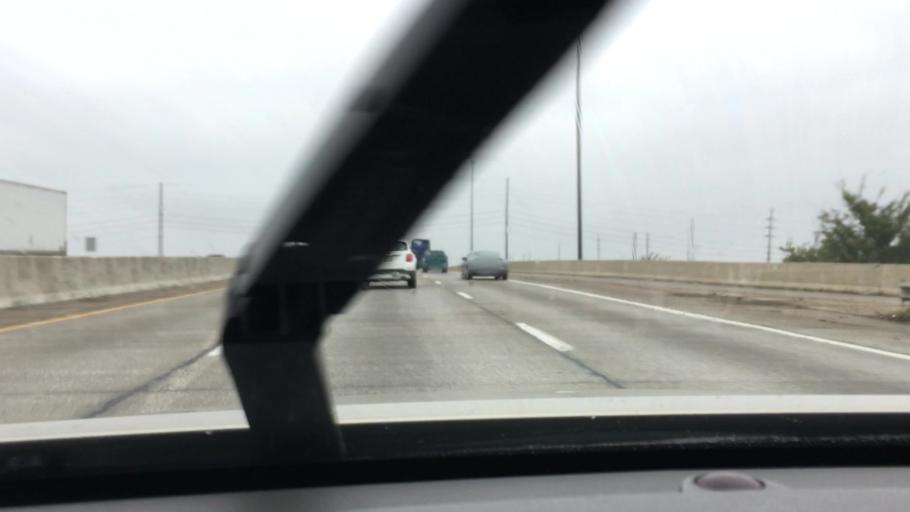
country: US
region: Indiana
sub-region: Marion County
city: Indianapolis
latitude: 39.7538
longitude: -86.1640
